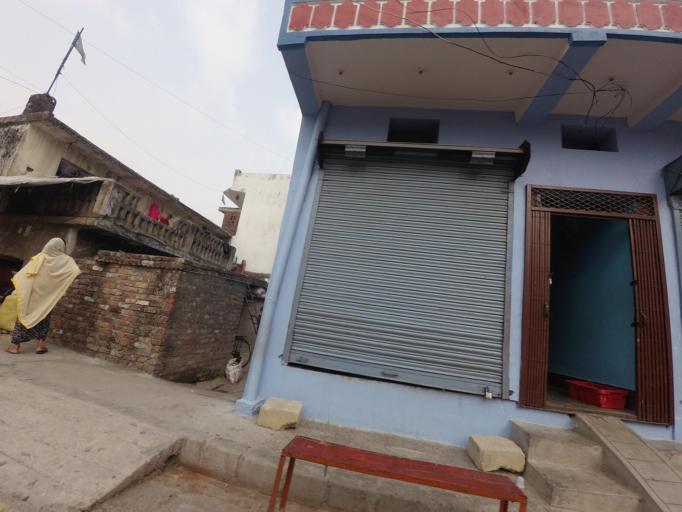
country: NP
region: Western Region
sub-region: Lumbini Zone
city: Bhairahawa
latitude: 27.4935
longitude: 83.4484
